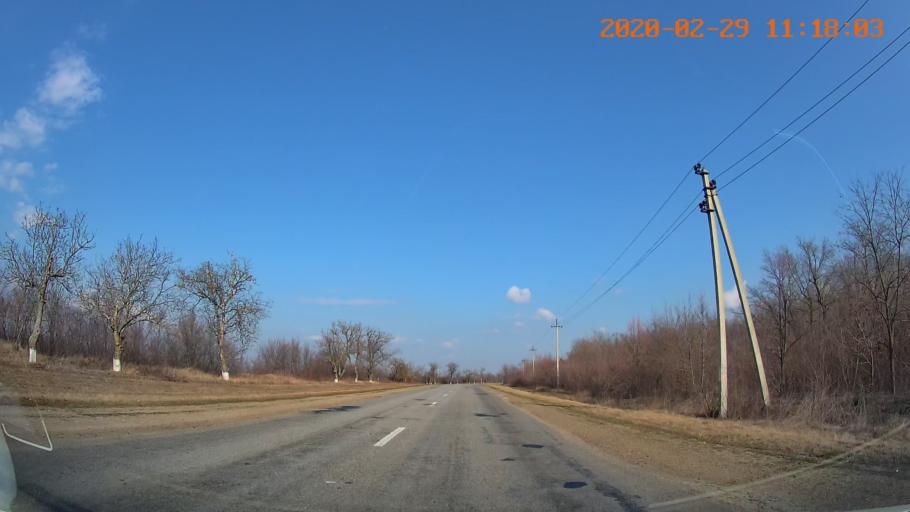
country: MD
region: Telenesti
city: Dubasari
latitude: 47.3297
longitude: 29.1719
